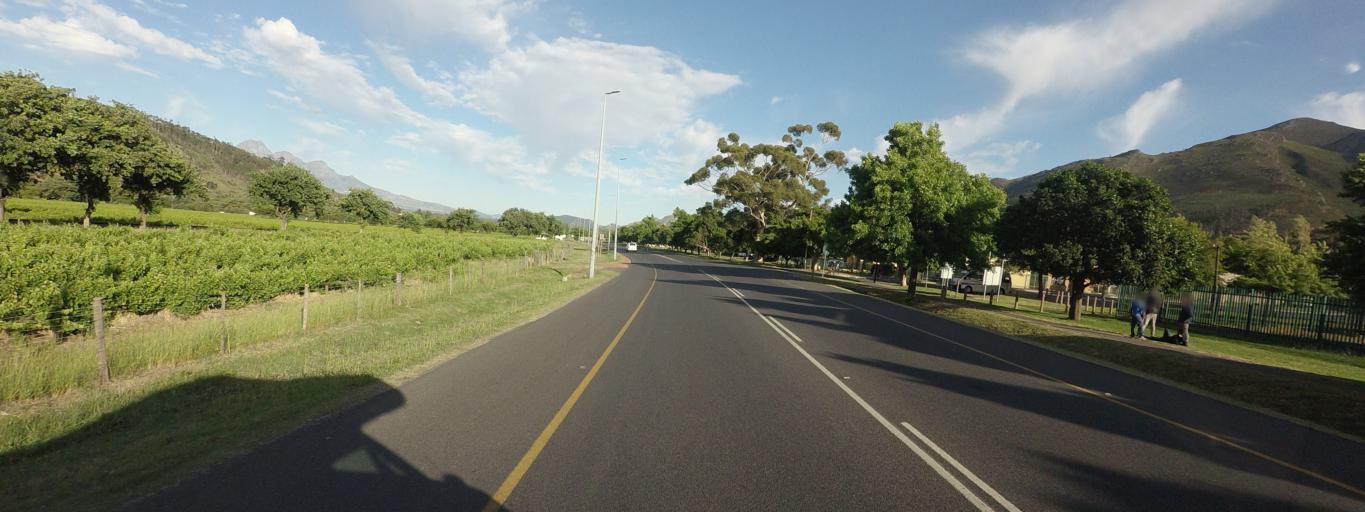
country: ZA
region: Western Cape
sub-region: Cape Winelands District Municipality
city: Paarl
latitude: -33.8958
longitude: 19.1000
